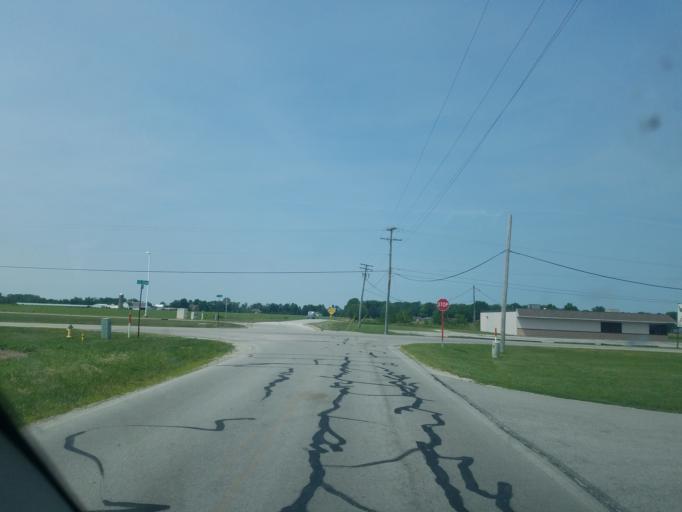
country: US
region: Ohio
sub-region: Seneca County
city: Tiffin
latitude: 41.1074
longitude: -83.2282
